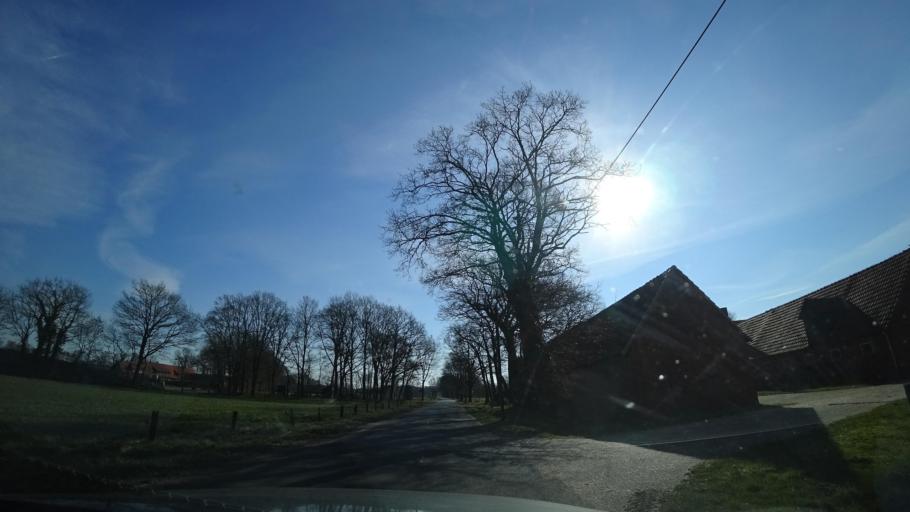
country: DE
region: Lower Saxony
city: Hatten
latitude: 53.0538
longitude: 8.3434
